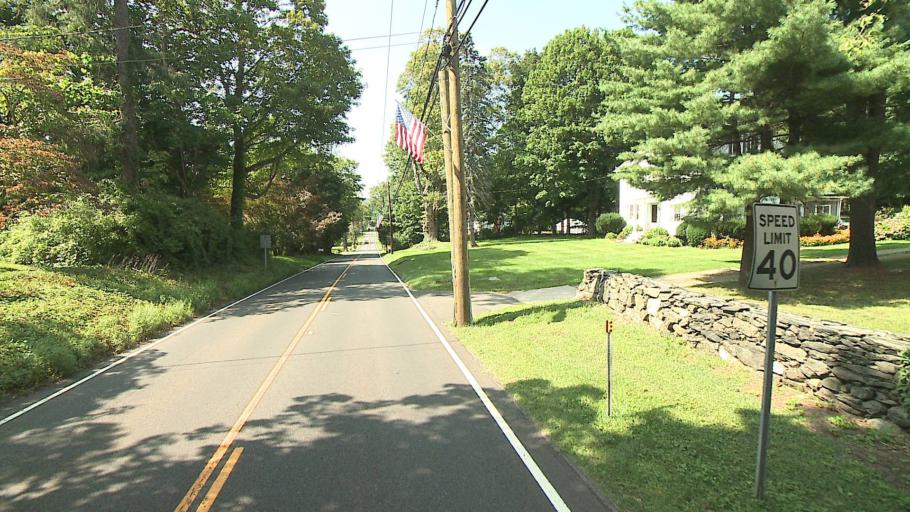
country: US
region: Connecticut
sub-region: Fairfield County
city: Danbury
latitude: 41.4720
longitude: -73.3928
